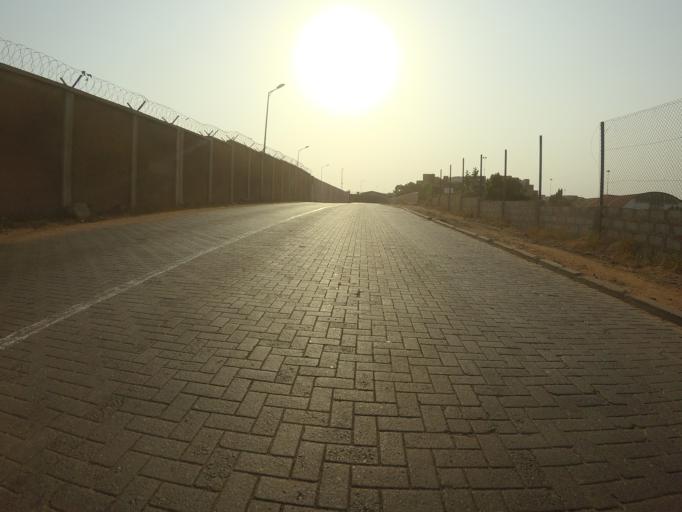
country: GH
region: Greater Accra
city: Tema
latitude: 5.6259
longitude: -0.0035
